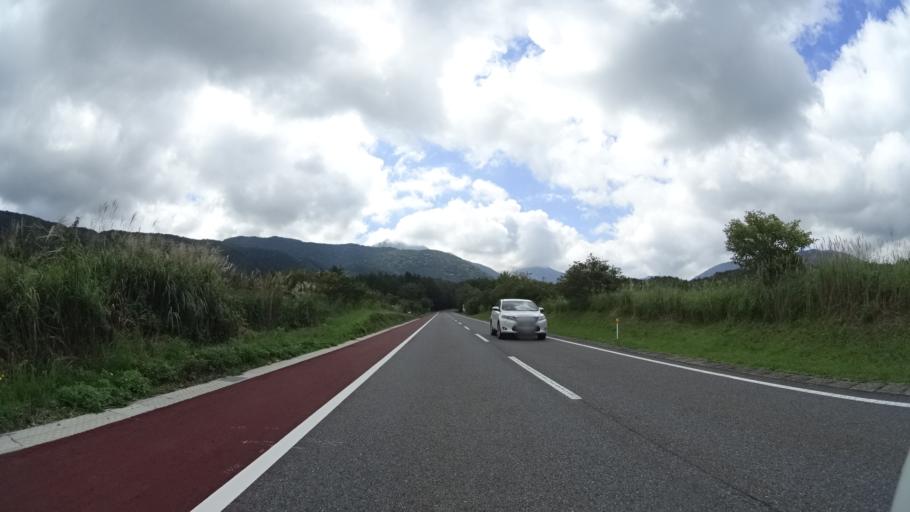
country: JP
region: Oita
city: Tsukawaki
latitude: 33.1403
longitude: 131.2402
